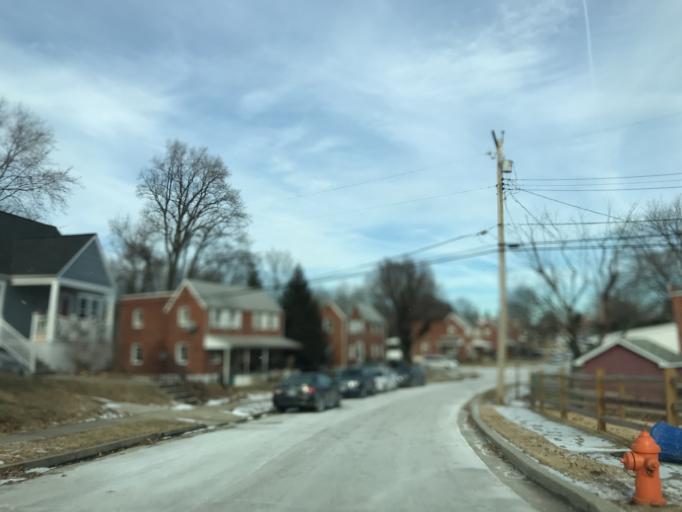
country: US
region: Maryland
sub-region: Baltimore County
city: Overlea
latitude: 39.3558
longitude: -76.5222
